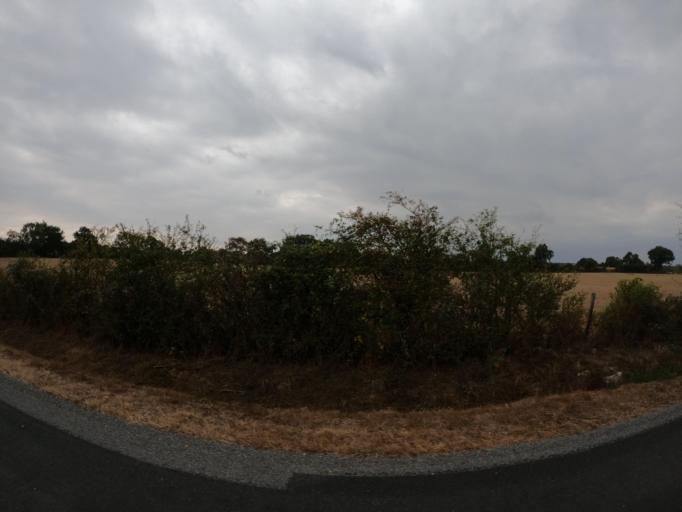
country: FR
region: Pays de la Loire
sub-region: Departement de la Vendee
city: Saint-Georges-de-Montaigu
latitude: 46.9710
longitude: -1.2804
